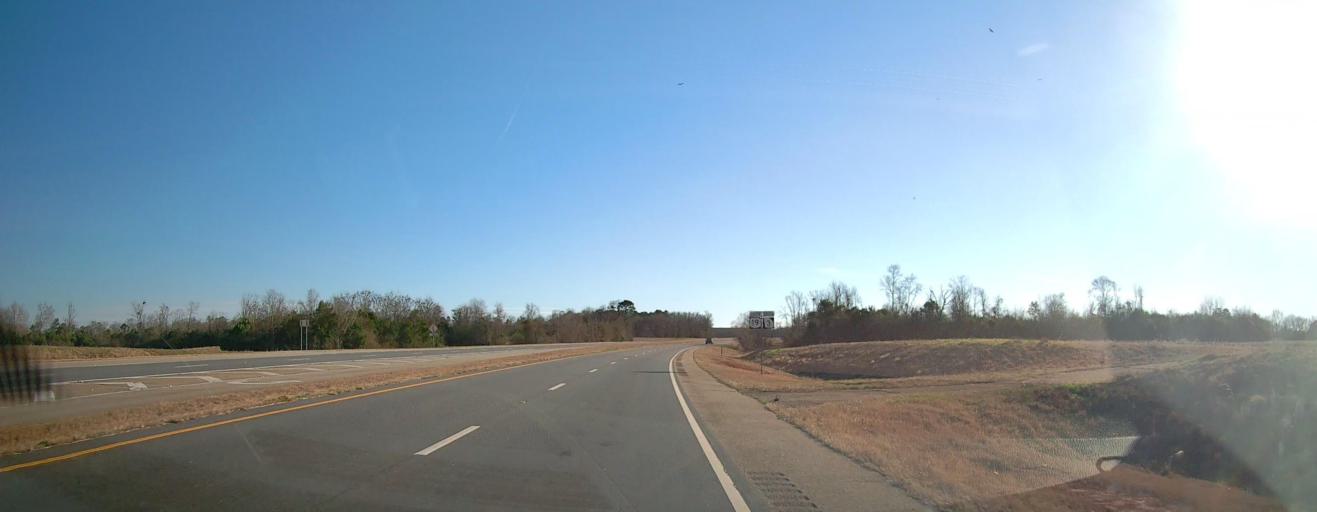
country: US
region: Georgia
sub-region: Sumter County
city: Americus
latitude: 31.9099
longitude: -84.2598
